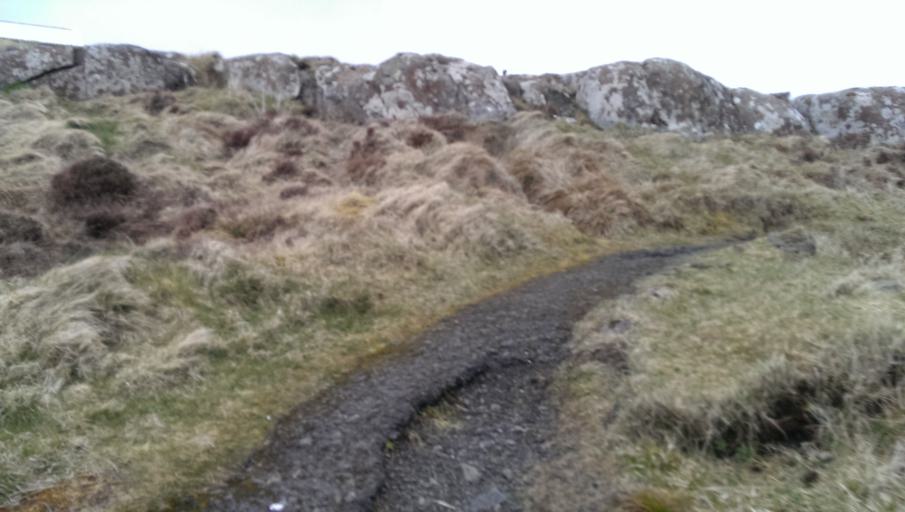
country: FO
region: Streymoy
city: Hoyvik
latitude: 62.0331
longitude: -6.7920
